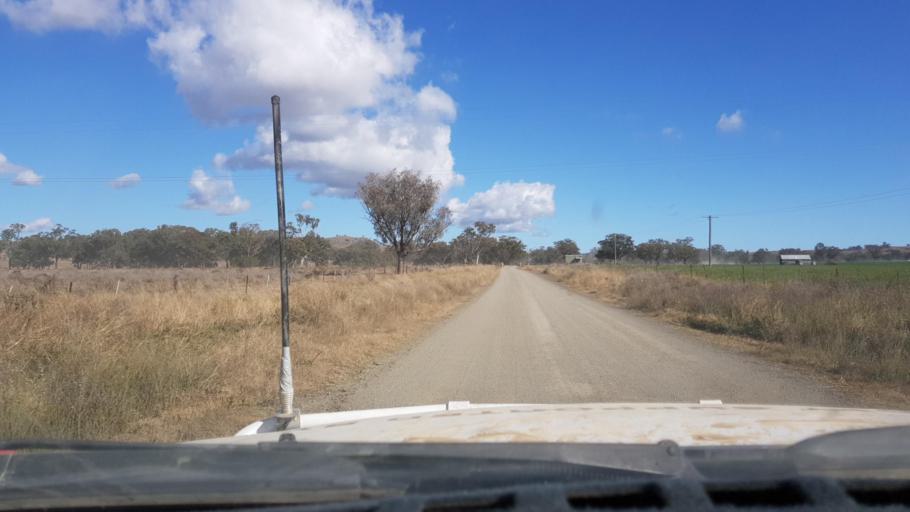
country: AU
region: New South Wales
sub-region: Tamworth Municipality
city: Manilla
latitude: -30.5847
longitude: 150.4832
